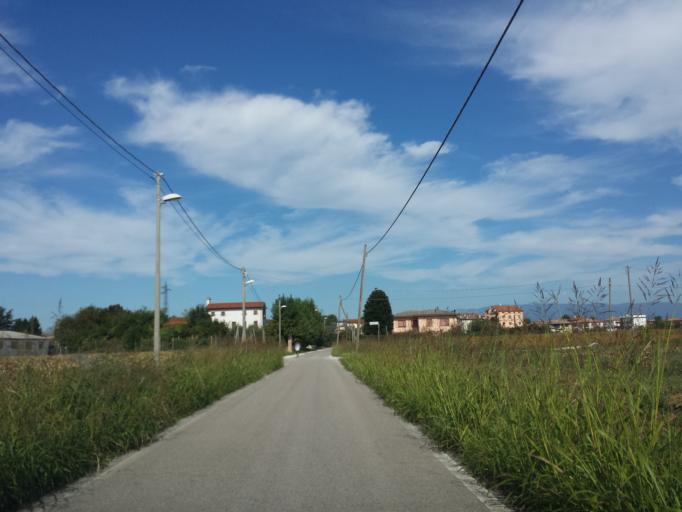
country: IT
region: Veneto
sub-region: Provincia di Vicenza
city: Vicenza
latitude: 45.5626
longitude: 11.5711
